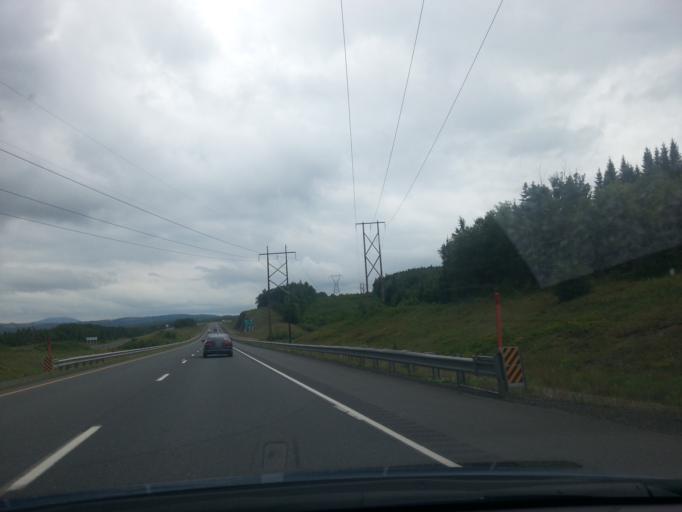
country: US
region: Maine
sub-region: Aroostook County
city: Limestone
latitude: 46.9978
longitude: -67.7314
